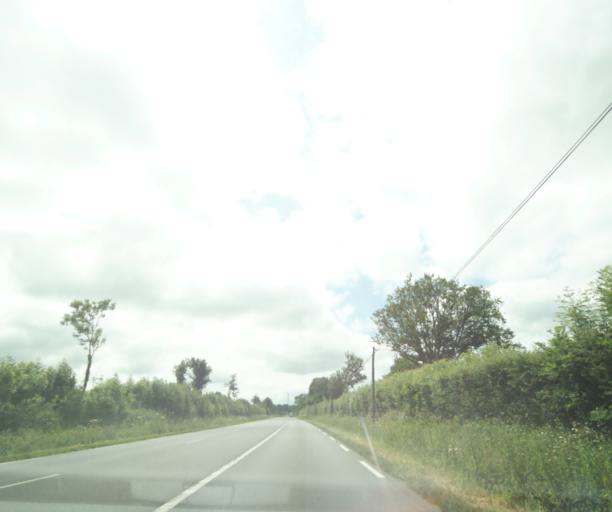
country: FR
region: Poitou-Charentes
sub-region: Departement des Deux-Sevres
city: Saint-Pardoux
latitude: 46.5861
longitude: -0.2925
